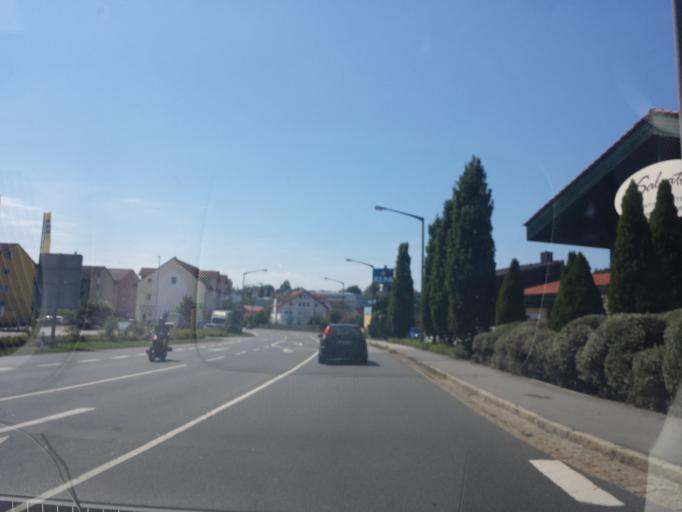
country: DE
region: Bavaria
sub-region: Upper Palatinate
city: Cham
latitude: 49.2280
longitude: 12.6737
